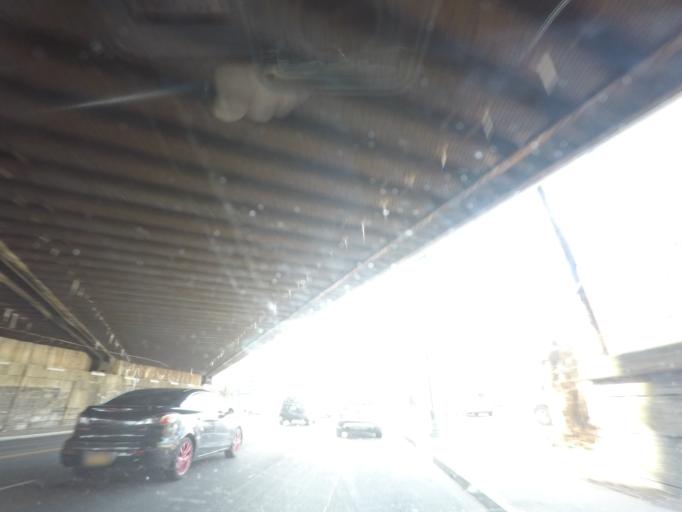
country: US
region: New York
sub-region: Schenectady County
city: Schenectady
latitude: 42.8169
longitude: -73.9414
